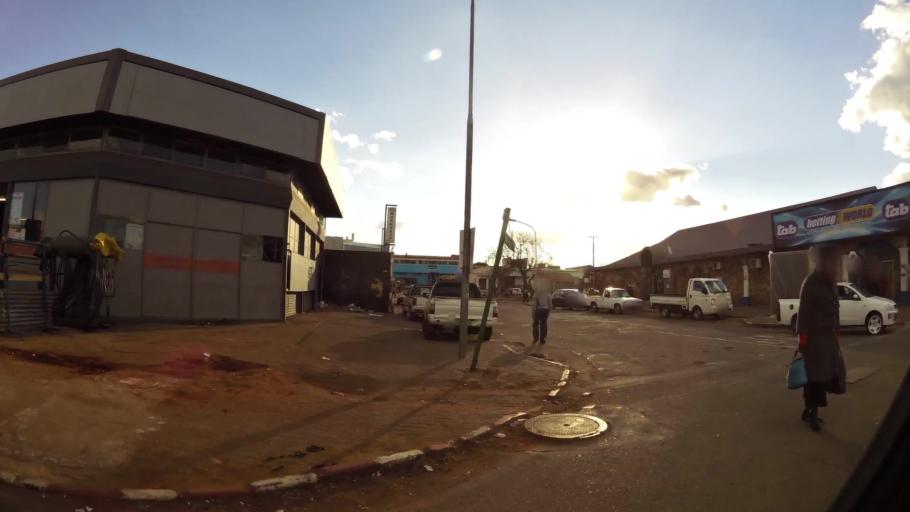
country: ZA
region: North-West
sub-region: Dr Kenneth Kaunda District Municipality
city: Potchefstroom
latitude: -26.7138
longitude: 27.0990
